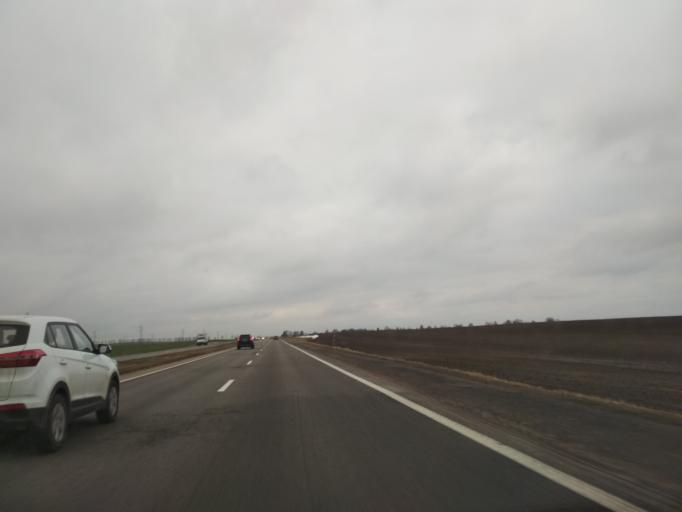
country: BY
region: Minsk
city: Mar''ina Horka
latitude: 53.5998
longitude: 28.0859
